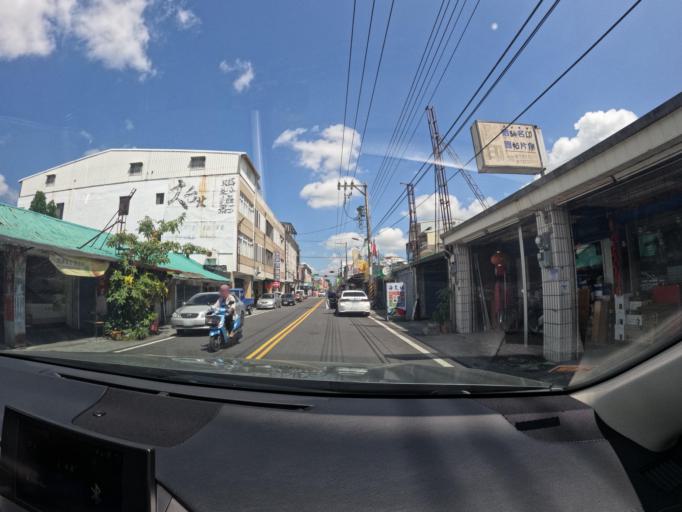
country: TW
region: Taiwan
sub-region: Hualien
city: Hualian
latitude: 23.6651
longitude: 121.4233
